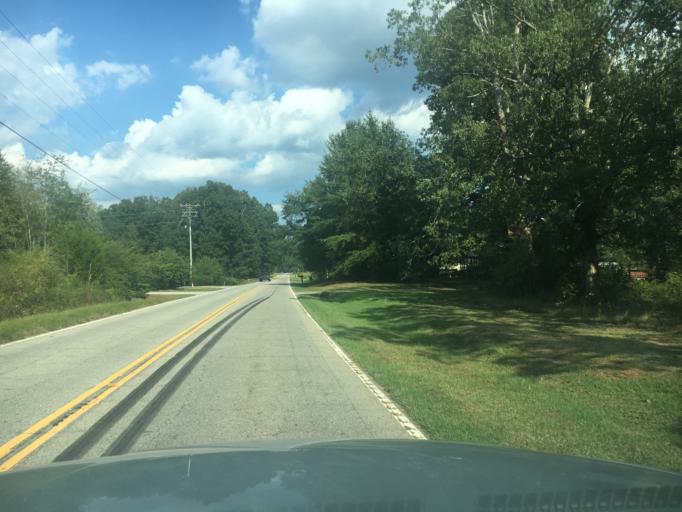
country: US
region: South Carolina
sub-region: Pickens County
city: Easley
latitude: 34.7166
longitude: -82.5873
